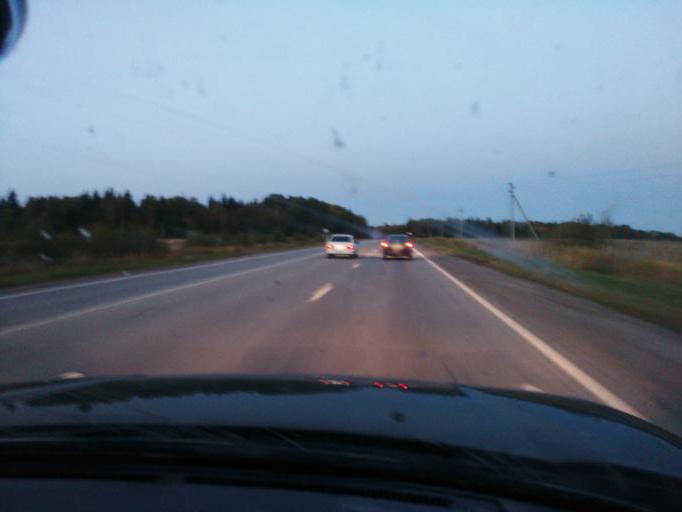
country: RU
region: Perm
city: Kalino
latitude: 58.2686
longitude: 57.3552
